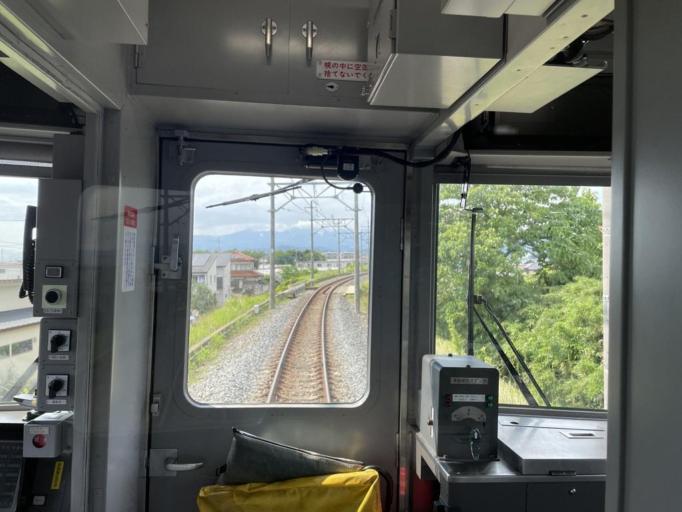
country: JP
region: Gunma
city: Kiryu
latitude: 36.4018
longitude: 139.3134
